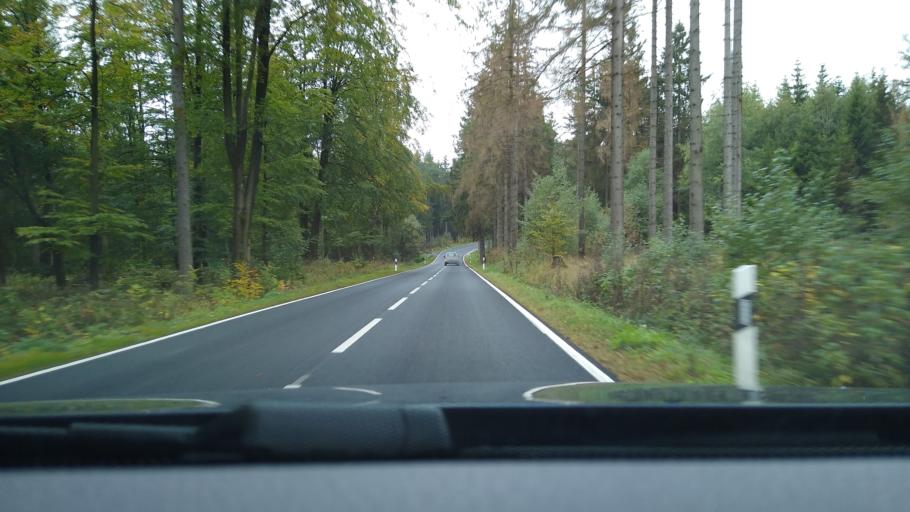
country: DE
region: Saxony-Anhalt
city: Elbingerode
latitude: 51.7729
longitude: 10.7641
